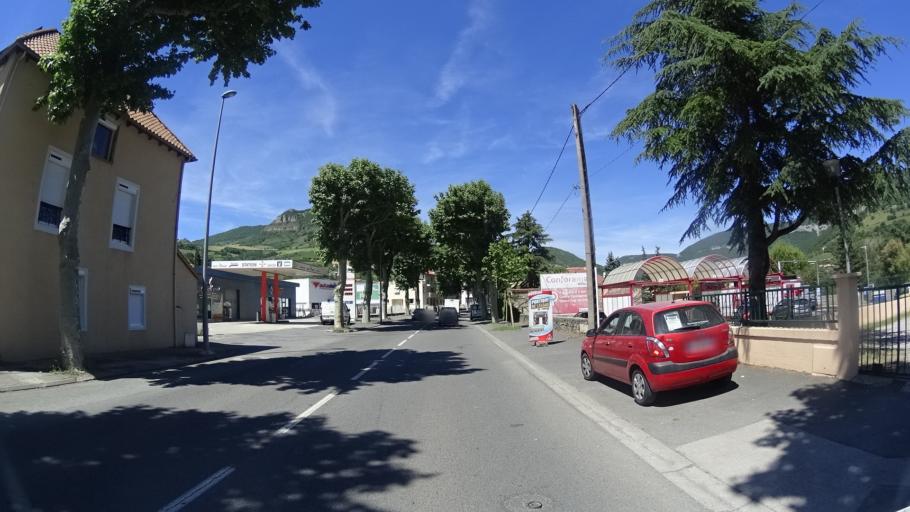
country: FR
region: Midi-Pyrenees
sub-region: Departement de l'Aveyron
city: Millau
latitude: 44.1132
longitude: 3.0827
